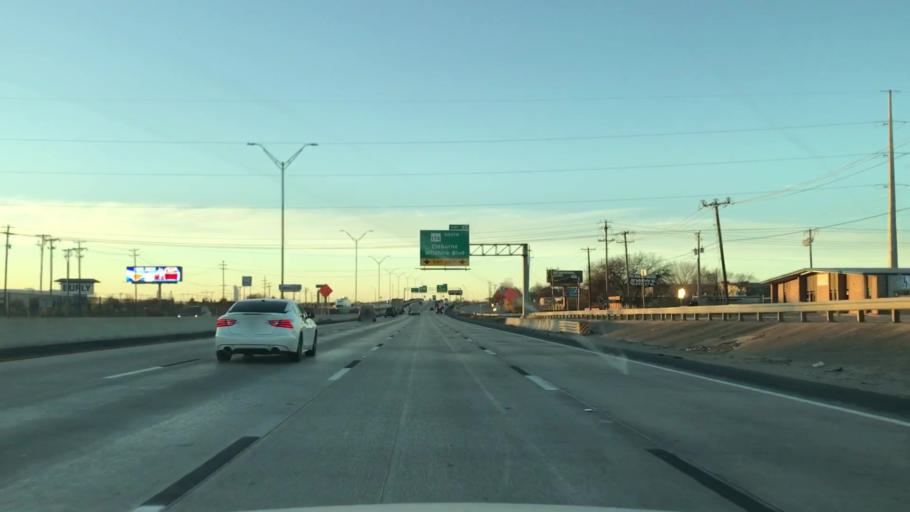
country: US
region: Texas
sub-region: Johnson County
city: Burleson
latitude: 32.5597
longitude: -97.3190
